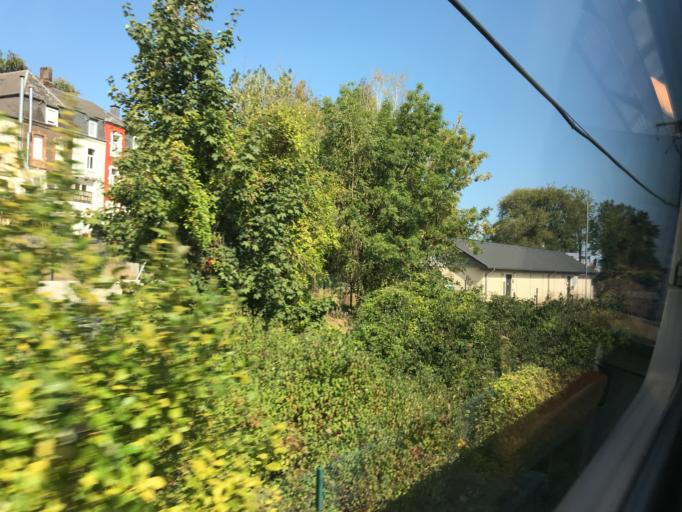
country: LU
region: Luxembourg
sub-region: Canton d'Esch-sur-Alzette
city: Niedercorn
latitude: 49.5321
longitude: 5.8925
